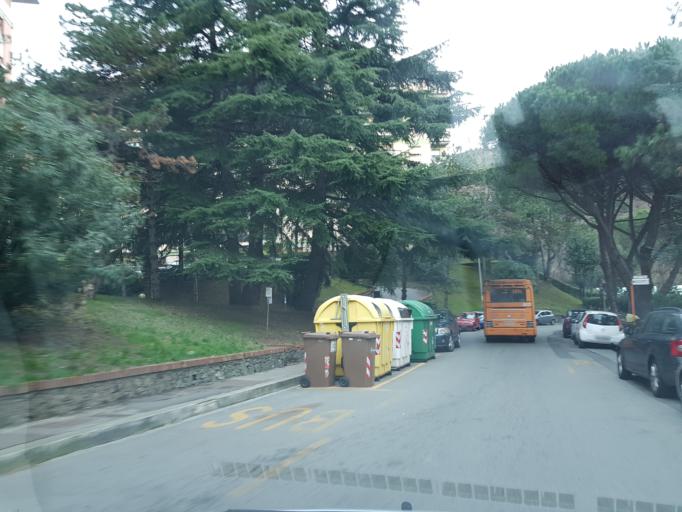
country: IT
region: Liguria
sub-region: Provincia di Genova
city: Mele
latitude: 44.4297
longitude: 8.8062
